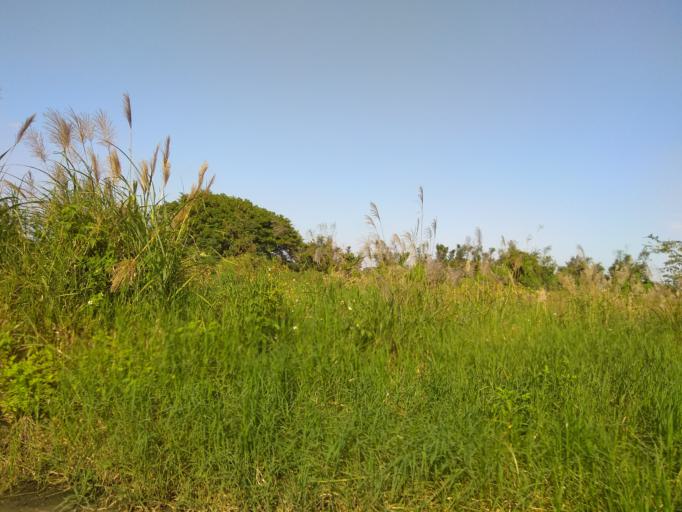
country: TW
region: Taiwan
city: Taoyuan City
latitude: 25.0500
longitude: 121.2295
